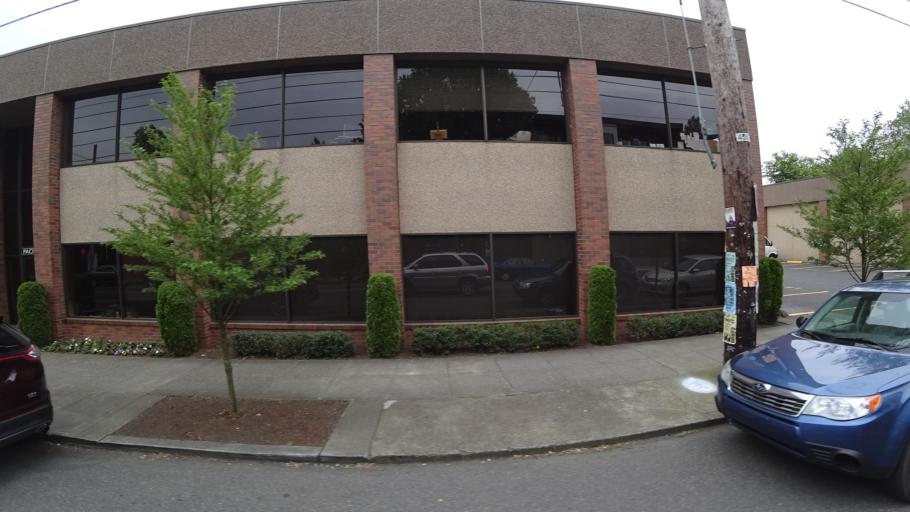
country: US
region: Oregon
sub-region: Multnomah County
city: Portland
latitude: 45.5193
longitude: -122.6355
